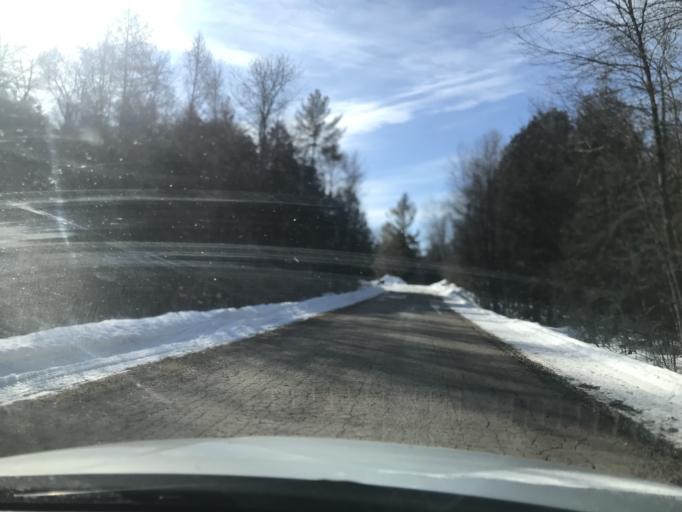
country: US
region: Wisconsin
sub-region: Oconto County
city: Gillett
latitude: 44.9586
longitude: -88.2754
